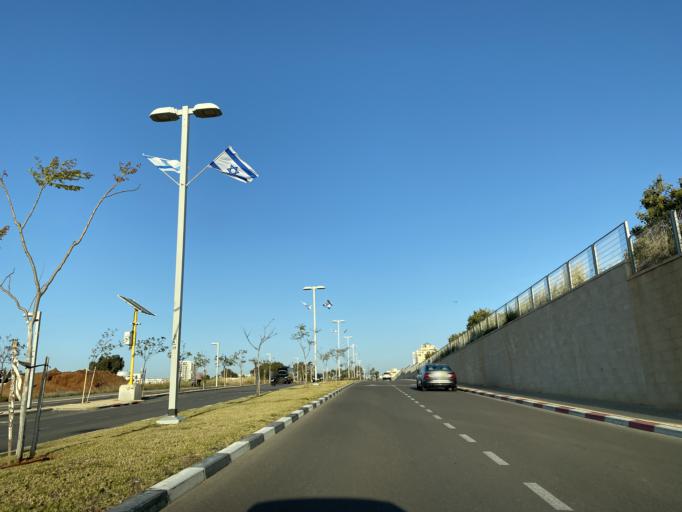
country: IL
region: Tel Aviv
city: Herzliyya
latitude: 32.1602
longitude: 34.8317
